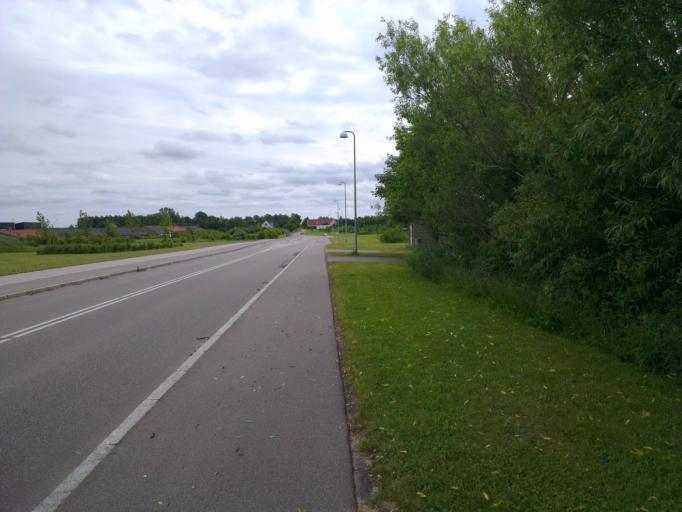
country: DK
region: Capital Region
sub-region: Frederikssund Kommune
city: Frederikssund
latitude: 55.8196
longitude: 12.0752
